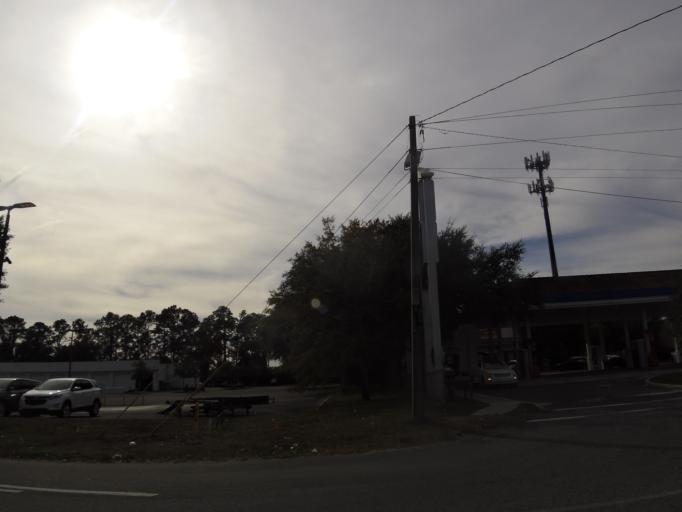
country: US
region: Florida
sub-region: Saint Johns County
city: Fruit Cove
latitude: 30.1778
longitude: -81.5515
